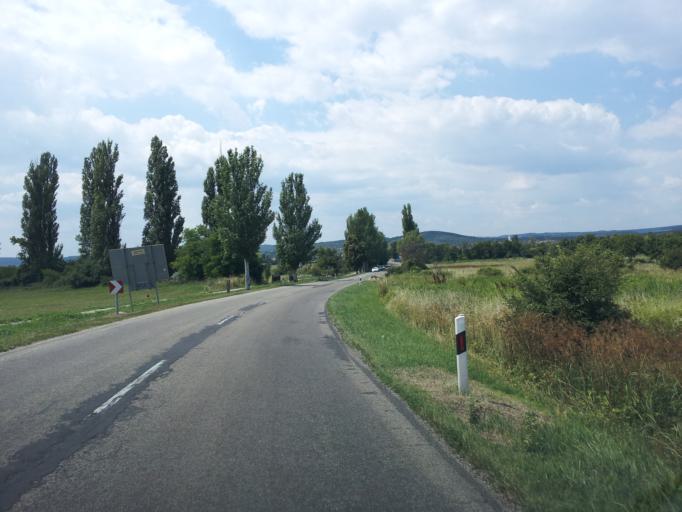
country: HU
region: Veszprem
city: Tihany
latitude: 46.9209
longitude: 17.8515
